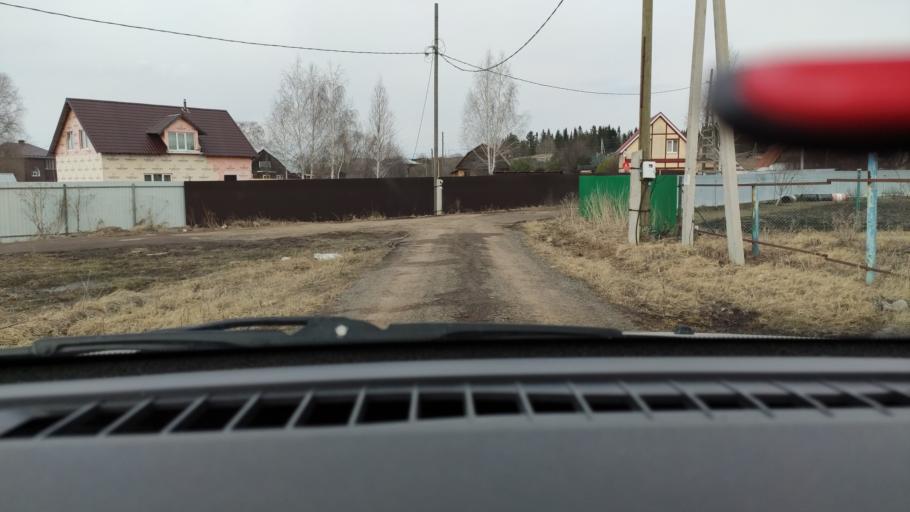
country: RU
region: Perm
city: Kultayevo
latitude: 57.8955
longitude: 56.0151
